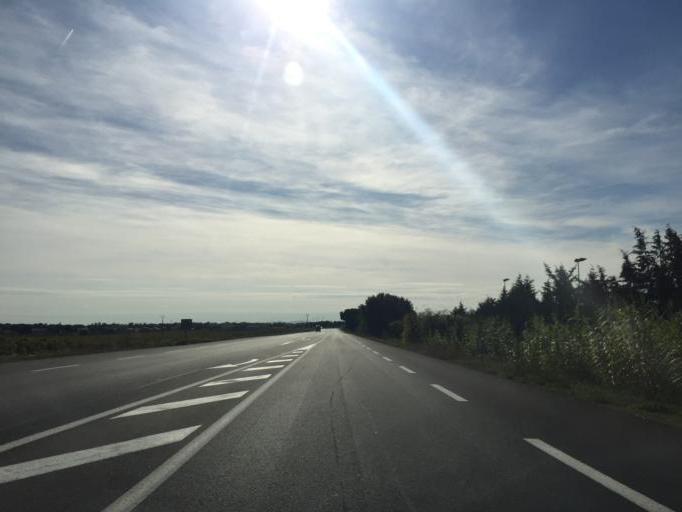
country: FR
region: Rhone-Alpes
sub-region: Departement de la Drome
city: Donzere
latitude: 44.4346
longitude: 4.7156
